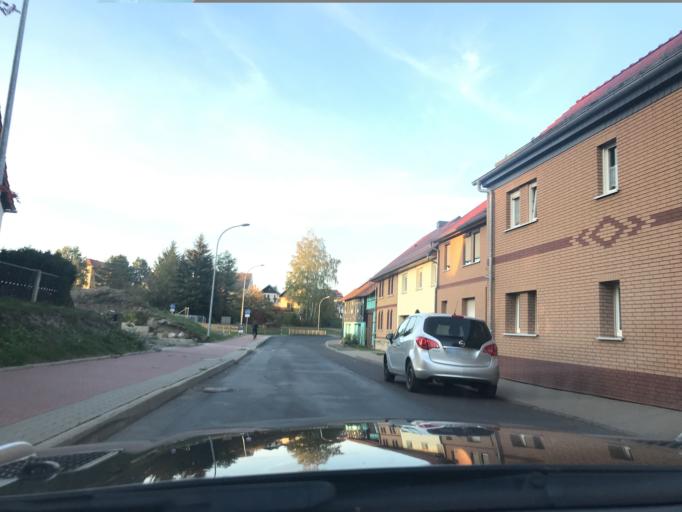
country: DE
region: Thuringia
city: Niederdorla
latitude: 51.1593
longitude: 10.4419
